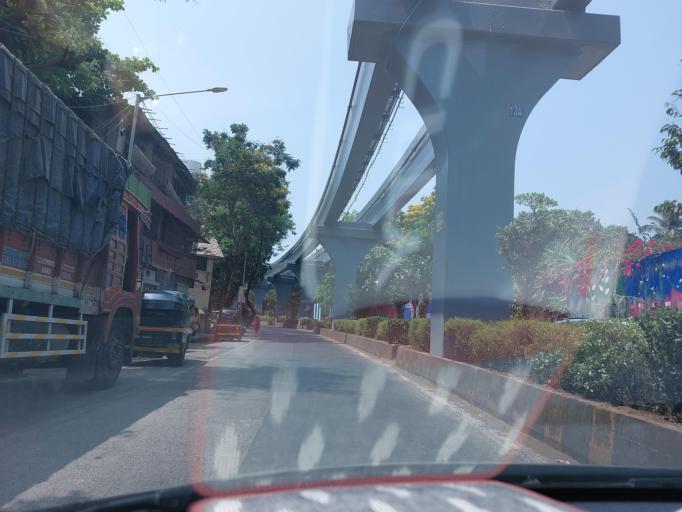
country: IN
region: Maharashtra
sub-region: Mumbai Suburban
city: Mumbai
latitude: 19.0586
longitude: 72.8958
